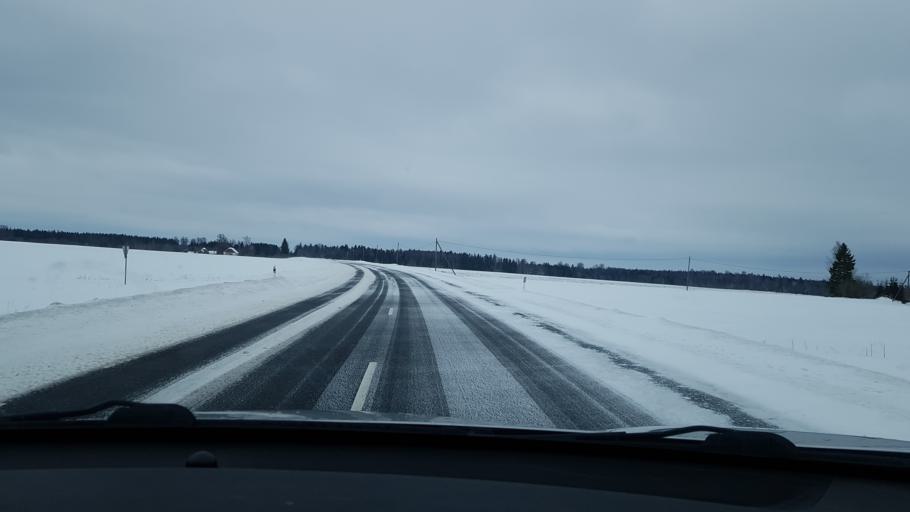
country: EE
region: Jaervamaa
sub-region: Jaerva-Jaani vald
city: Jarva-Jaani
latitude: 59.1110
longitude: 25.7974
